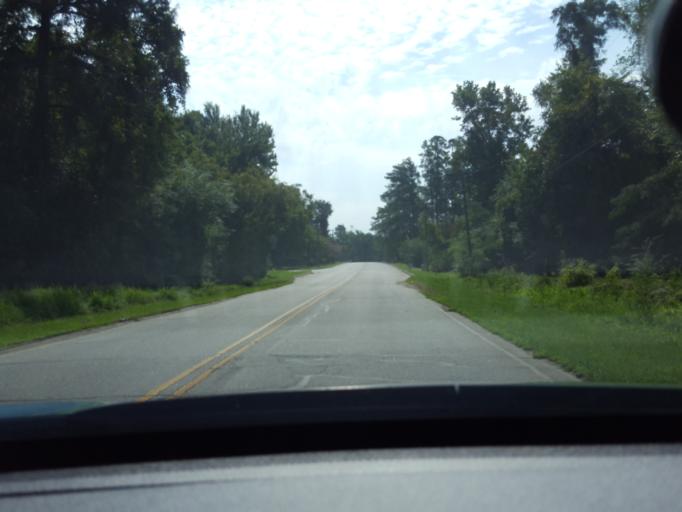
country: US
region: North Carolina
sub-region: Washington County
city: Plymouth
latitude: 35.8695
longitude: -76.7301
